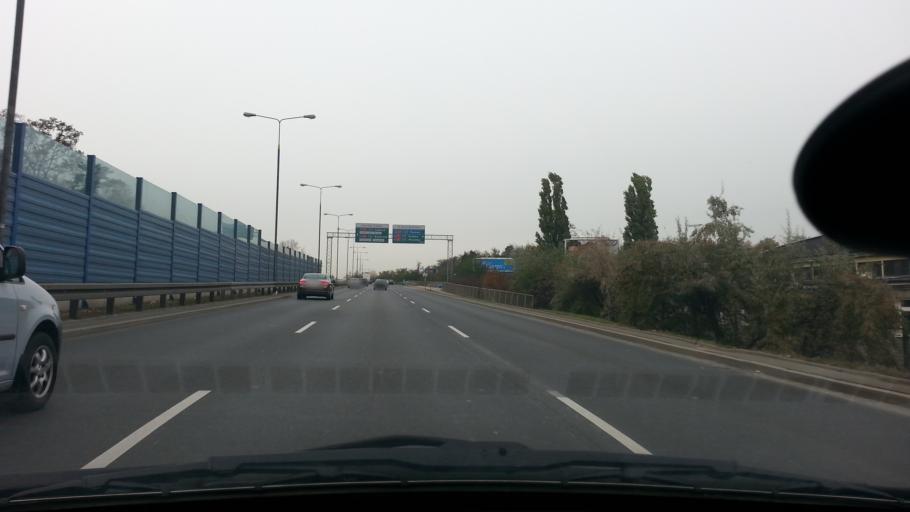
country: PL
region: Masovian Voivodeship
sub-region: Warszawa
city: Wola
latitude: 52.2505
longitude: 20.9559
